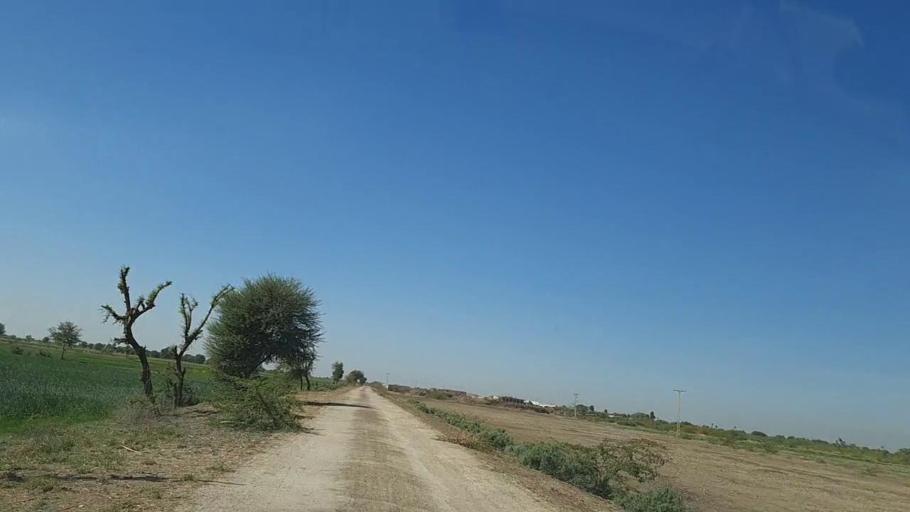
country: PK
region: Sindh
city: Dhoro Naro
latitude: 25.4890
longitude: 69.5156
